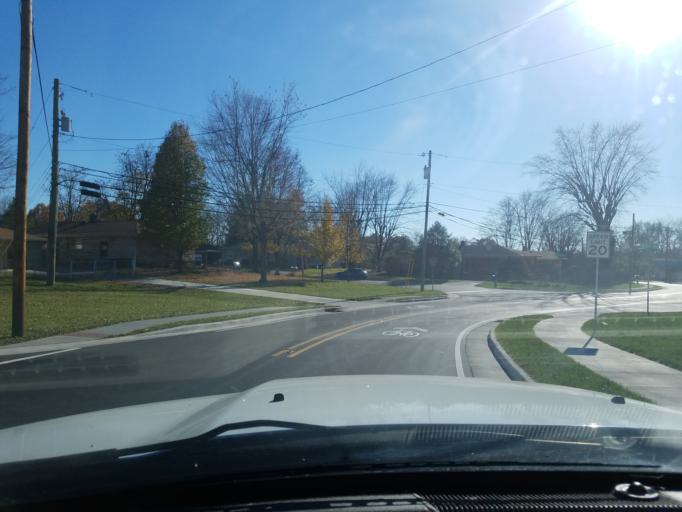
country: US
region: Indiana
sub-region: Floyd County
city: New Albany
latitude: 38.3213
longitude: -85.8137
